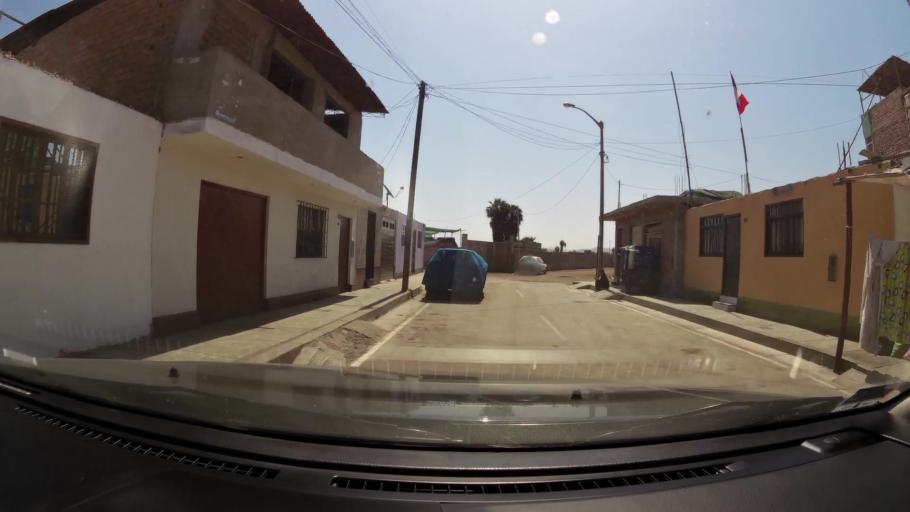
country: PE
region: Lima
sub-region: Provincia de Canete
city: San Vicente de Canete
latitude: -13.0215
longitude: -76.4775
